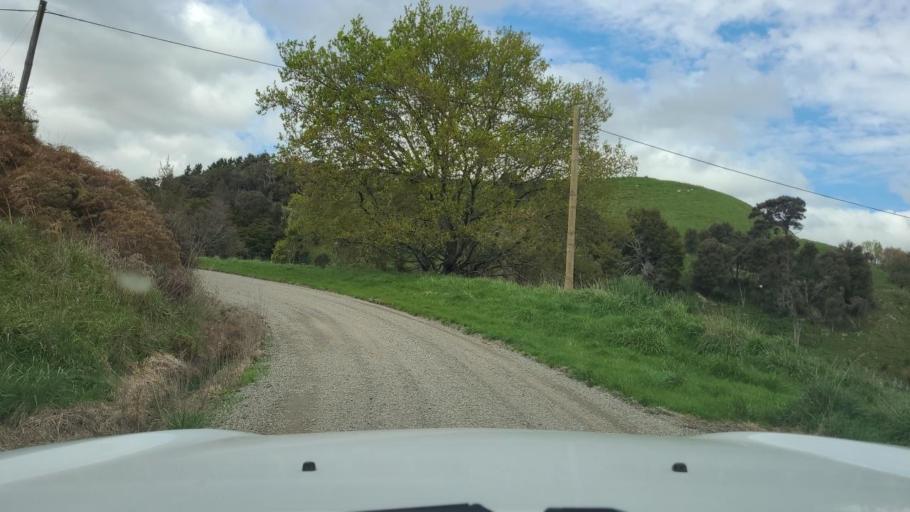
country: NZ
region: Wellington
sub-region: South Wairarapa District
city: Waipawa
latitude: -41.2147
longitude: 175.6051
